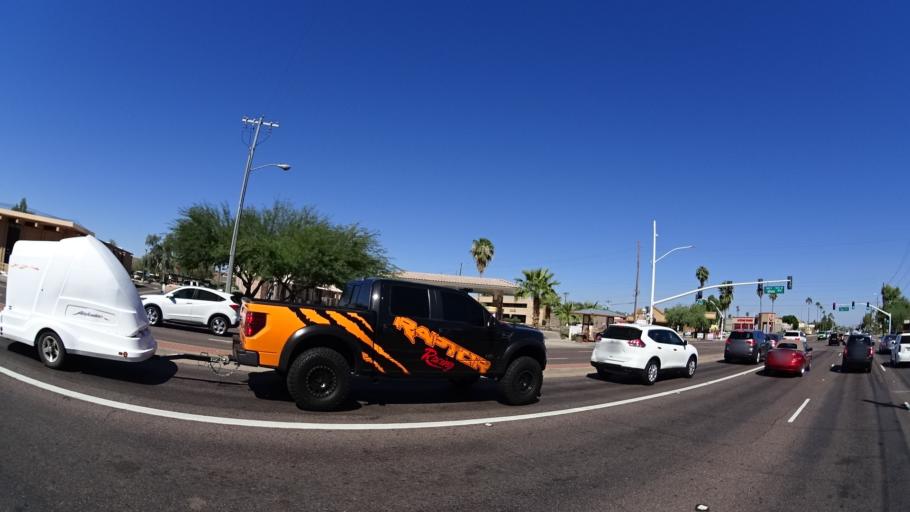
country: US
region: Arizona
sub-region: Maricopa County
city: Paradise Valley
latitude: 33.5815
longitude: -111.9259
